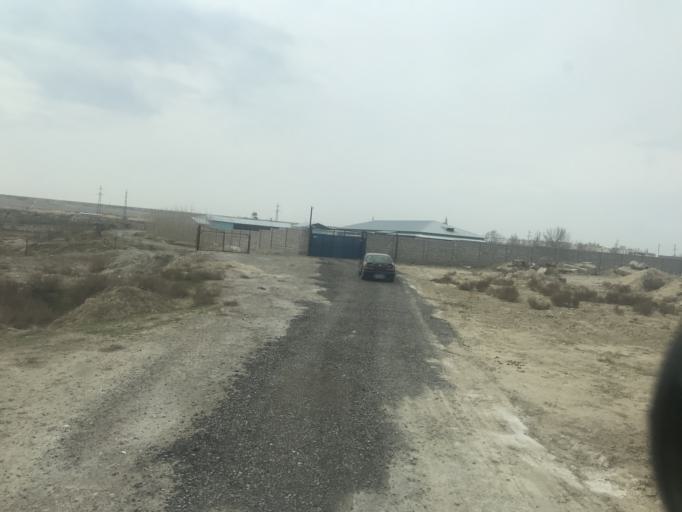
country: KZ
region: Ongtustik Qazaqstan
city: Shardara
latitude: 41.2561
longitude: 67.9279
